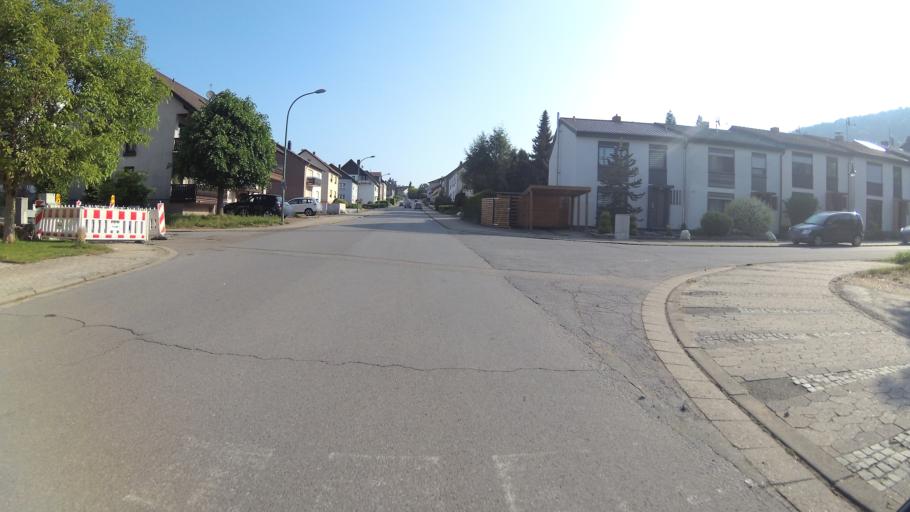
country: DE
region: Saarland
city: Kirkel
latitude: 49.2852
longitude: 7.2367
